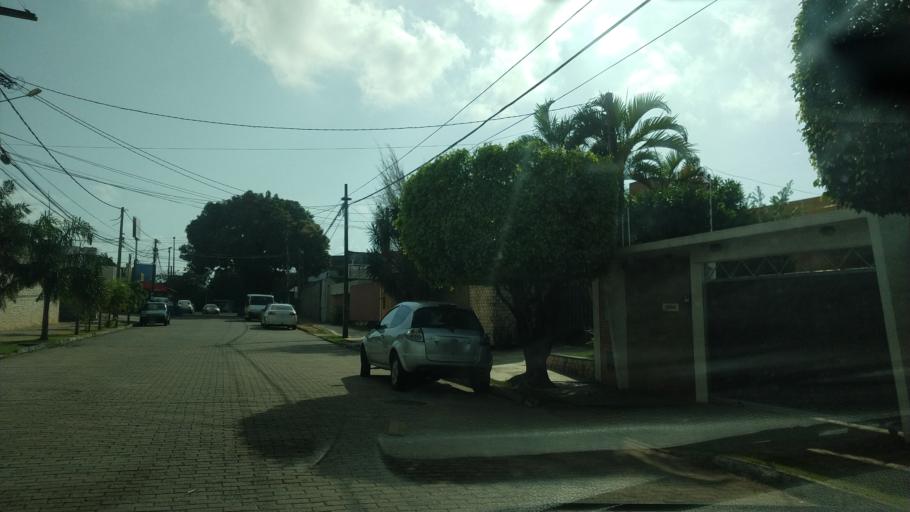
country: BR
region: Rio Grande do Norte
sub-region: Natal
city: Natal
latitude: -5.8560
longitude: -35.2004
